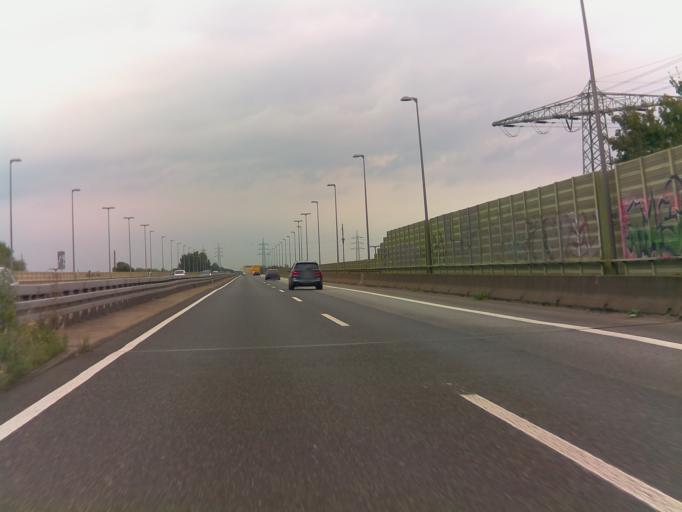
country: DE
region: Hesse
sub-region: Regierungsbezirk Darmstadt
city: Hanau am Main
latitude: 50.1047
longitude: 8.9171
